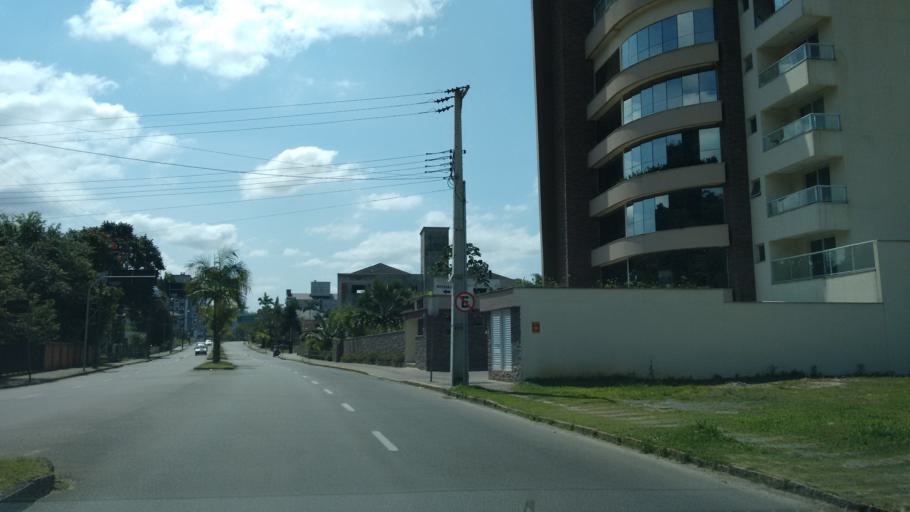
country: BR
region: Santa Catarina
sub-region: Pomerode
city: Pomerode
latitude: -26.7354
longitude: -49.1786
